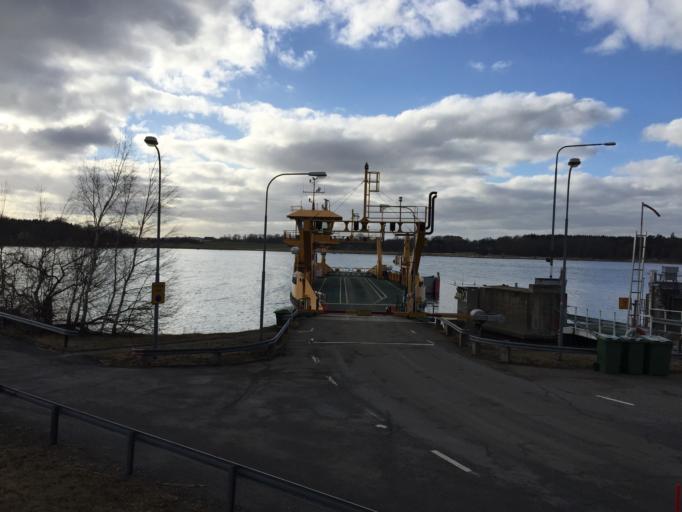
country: SE
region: Stockholm
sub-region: Sodertalje Kommun
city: Pershagen
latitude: 59.0524
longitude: 17.6937
